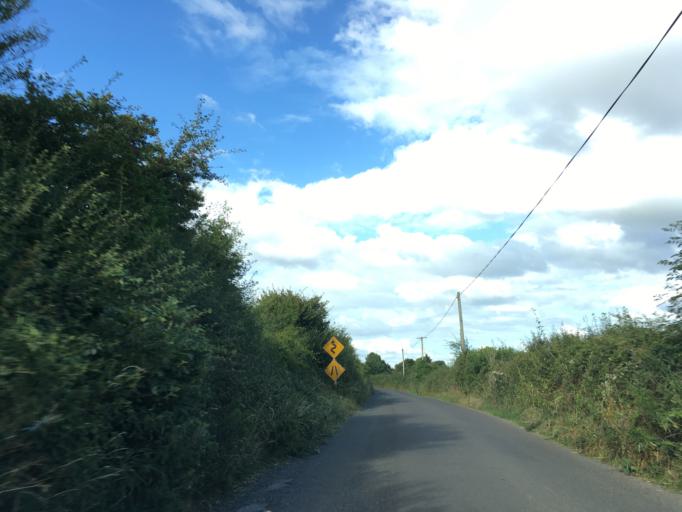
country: IE
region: Munster
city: Cahir
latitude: 52.2784
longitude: -7.9547
